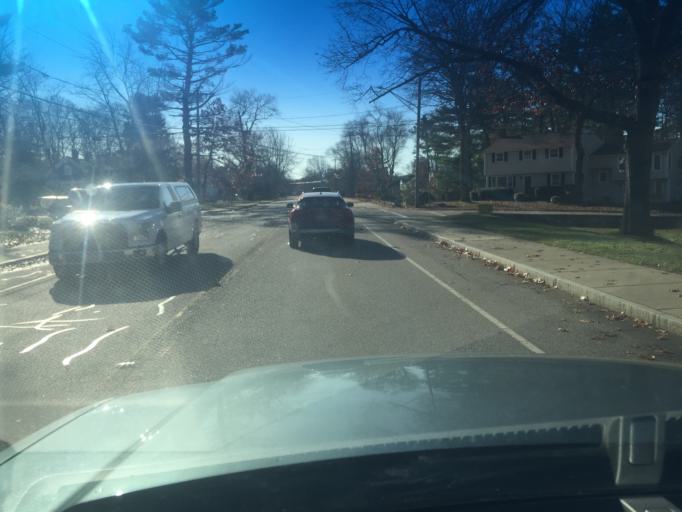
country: US
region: Massachusetts
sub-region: Norfolk County
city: Franklin
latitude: 42.1026
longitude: -71.4283
